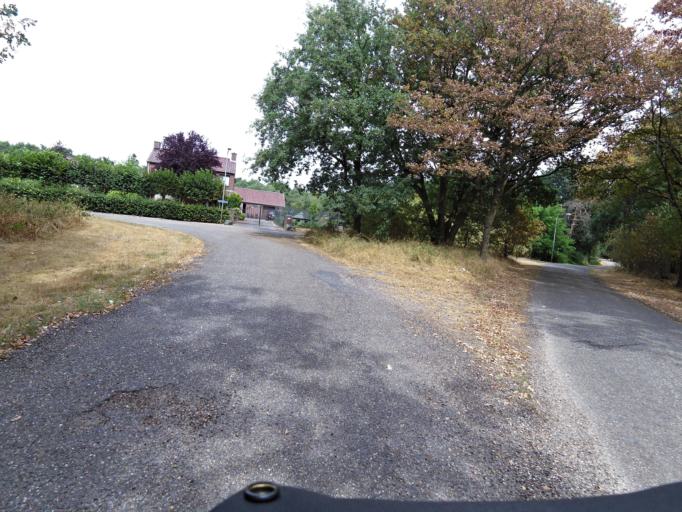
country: NL
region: Limburg
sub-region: Gemeente Bergen
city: Wellerlooi
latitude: 51.5557
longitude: 6.1122
